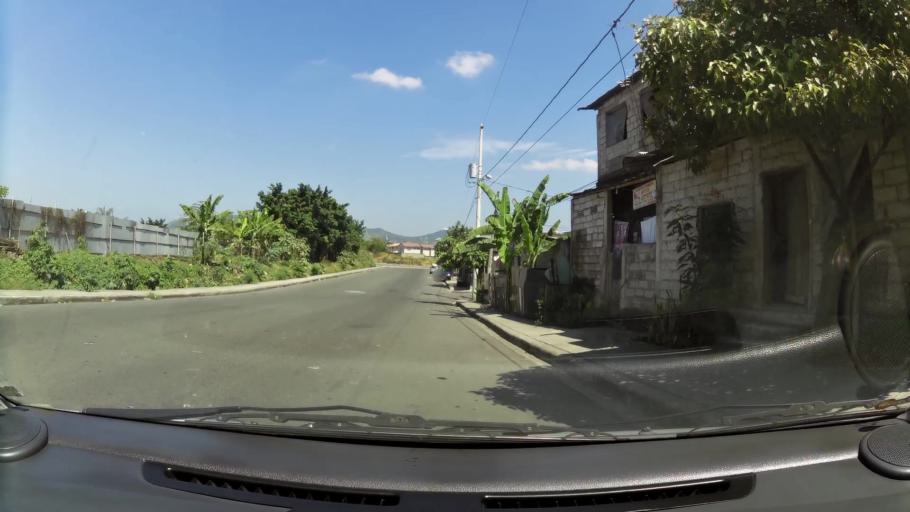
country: EC
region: Guayas
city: Guayaquil
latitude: -2.1299
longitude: -79.9262
